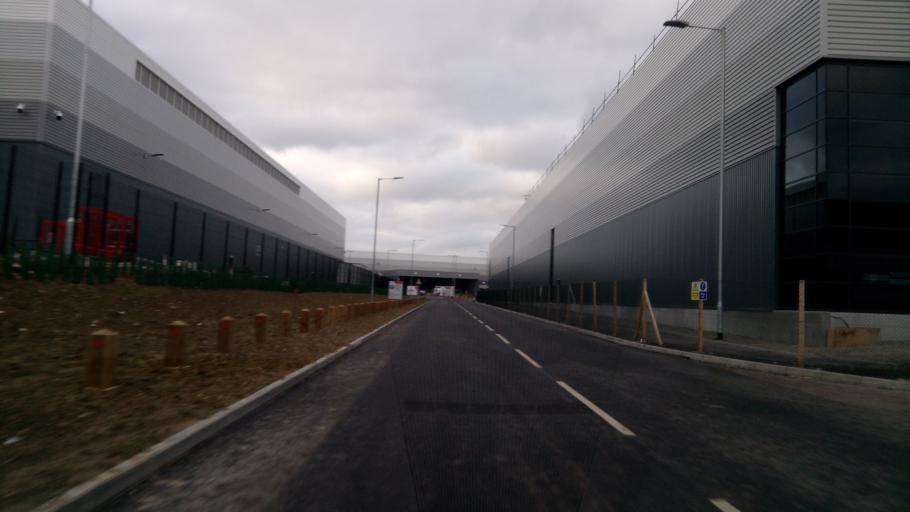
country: GB
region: England
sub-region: Cambridgeshire
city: Yaxley
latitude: 52.5320
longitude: -0.2989
